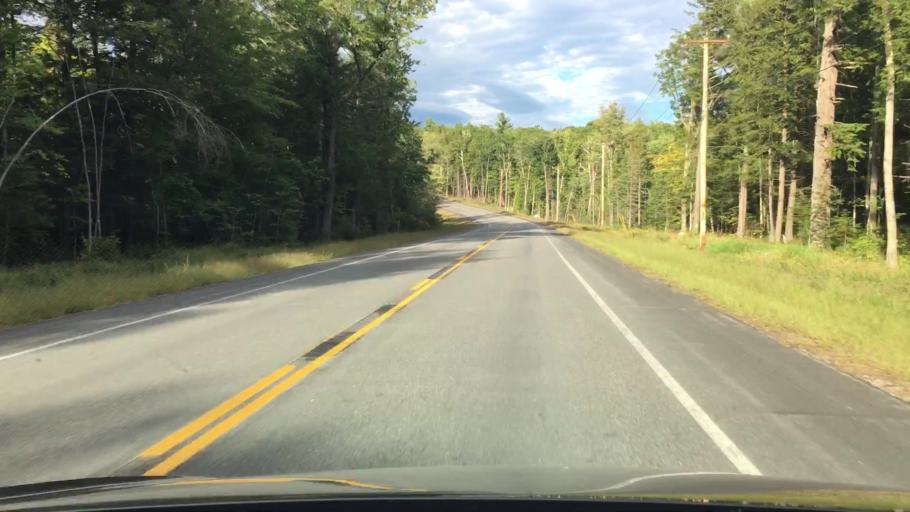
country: US
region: Maine
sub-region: Oxford County
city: Lovell
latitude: 44.0352
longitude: -70.8900
